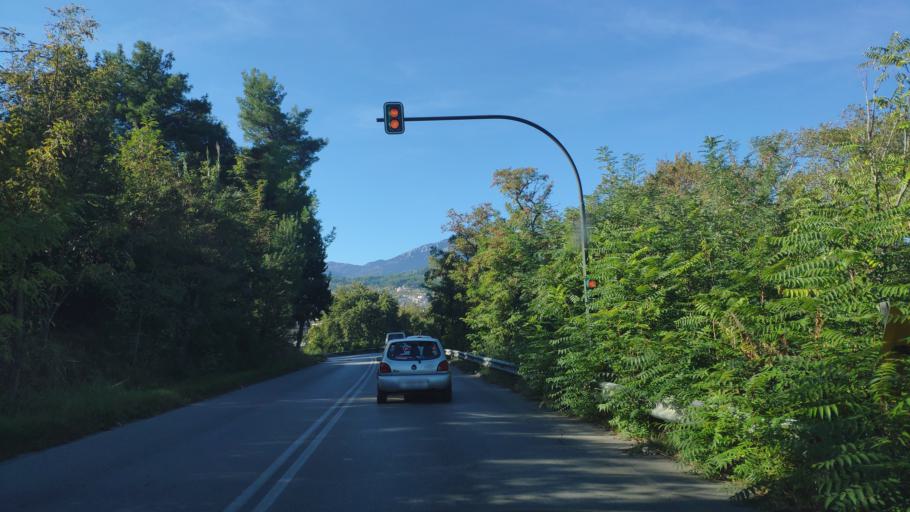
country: GR
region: Central Greece
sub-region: Nomos Voiotias
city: Livadeia
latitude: 38.4455
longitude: 22.8794
